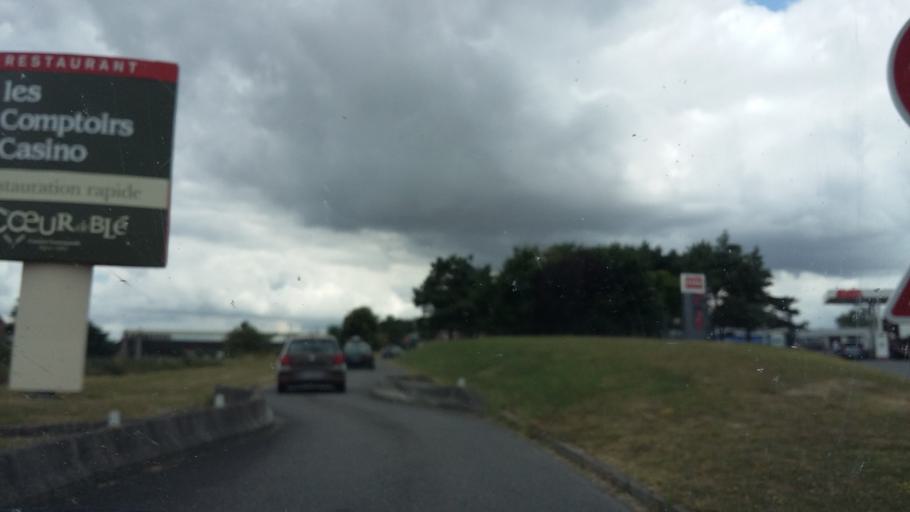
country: FR
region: Poitou-Charentes
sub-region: Departement de la Vienne
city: Antran
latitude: 46.9048
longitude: 0.5226
